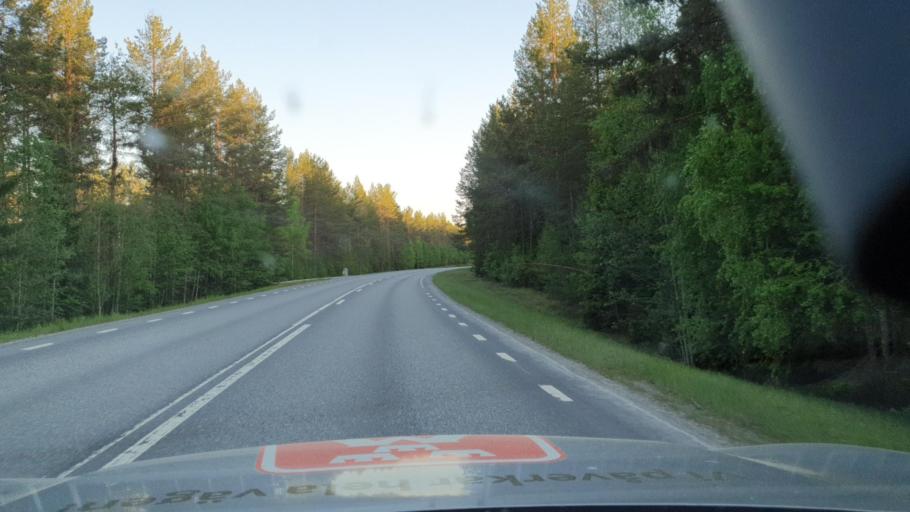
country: SE
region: Vaesternorrland
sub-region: Solleftea Kommun
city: Solleftea
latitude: 63.2567
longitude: 17.2188
